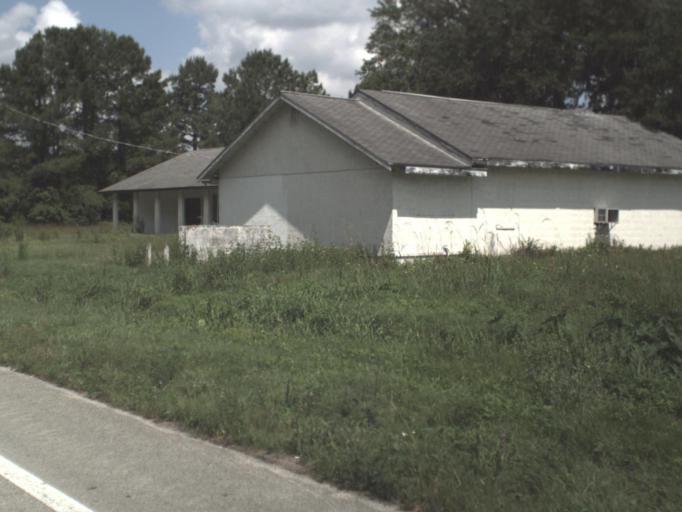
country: US
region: Florida
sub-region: Putnam County
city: East Palatka
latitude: 29.7255
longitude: -81.4787
